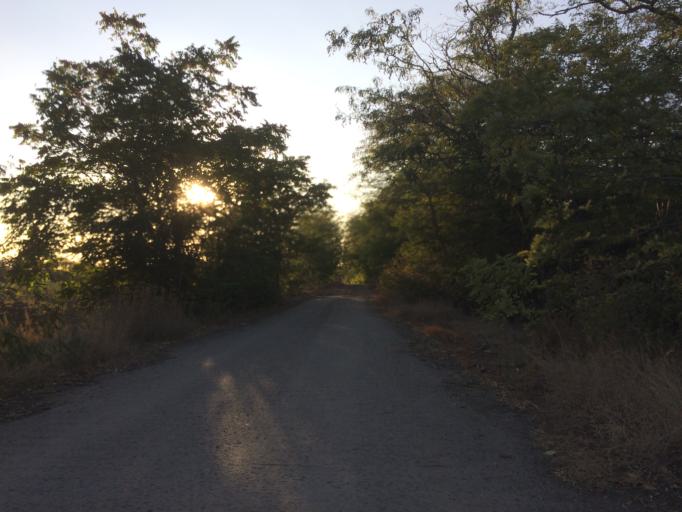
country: RU
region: Rostov
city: Gigant
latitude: 46.5094
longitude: 41.1914
